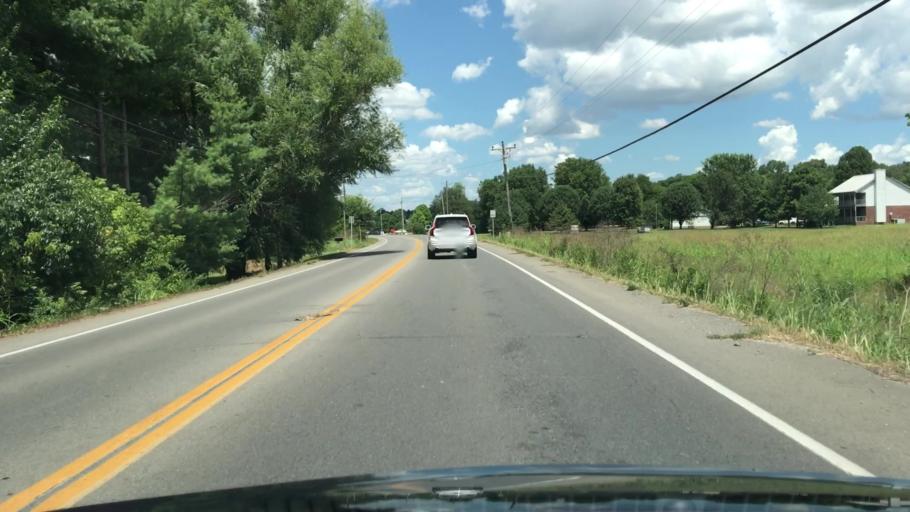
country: US
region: Tennessee
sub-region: Williamson County
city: Nolensville
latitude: 35.9830
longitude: -86.6787
